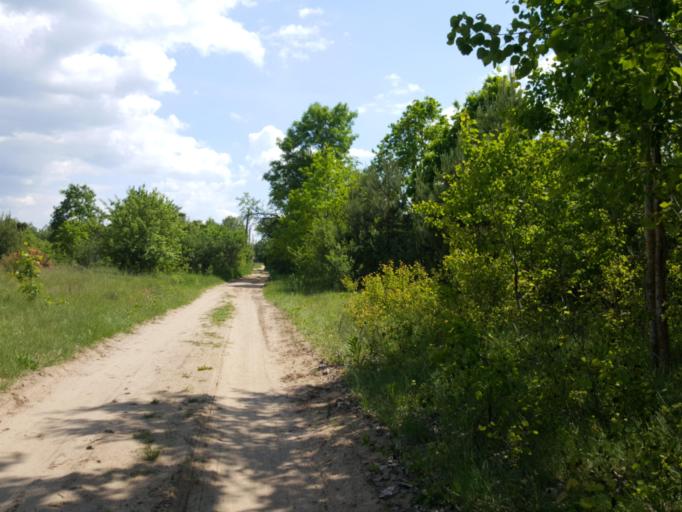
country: PL
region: Podlasie
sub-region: Powiat hajnowski
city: Hajnowka
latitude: 52.5730
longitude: 23.6271
